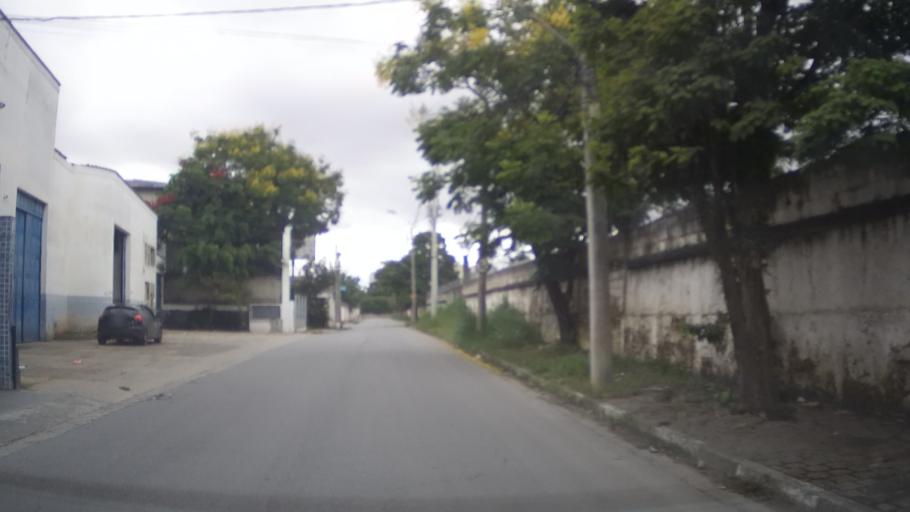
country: BR
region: Sao Paulo
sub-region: Guarulhos
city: Guarulhos
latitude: -23.4765
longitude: -46.5227
